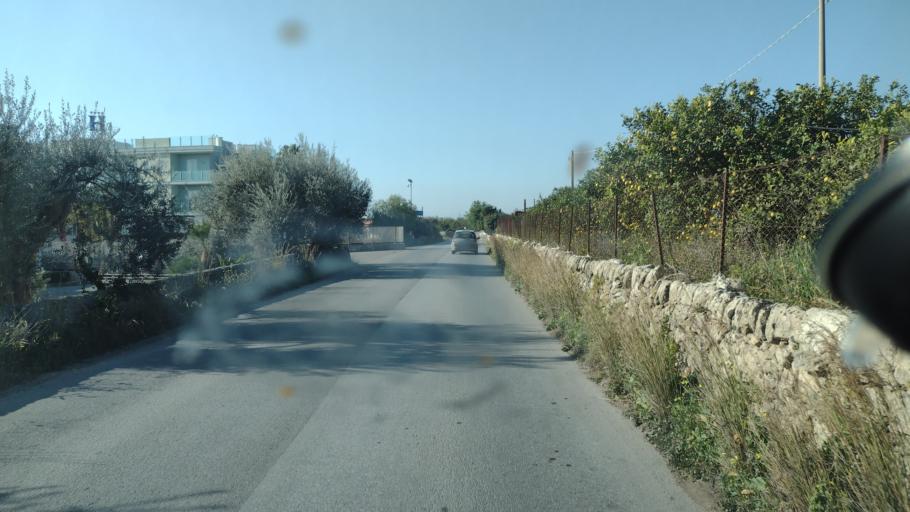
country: IT
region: Sicily
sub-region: Provincia di Siracusa
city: Avola
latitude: 36.8957
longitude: 15.1337
